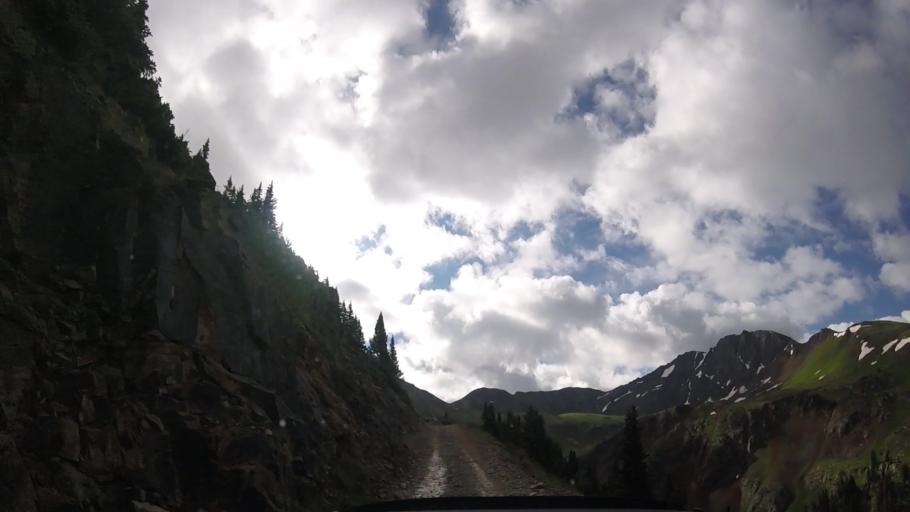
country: US
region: Colorado
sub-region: San Juan County
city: Silverton
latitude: 37.9128
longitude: -107.6344
